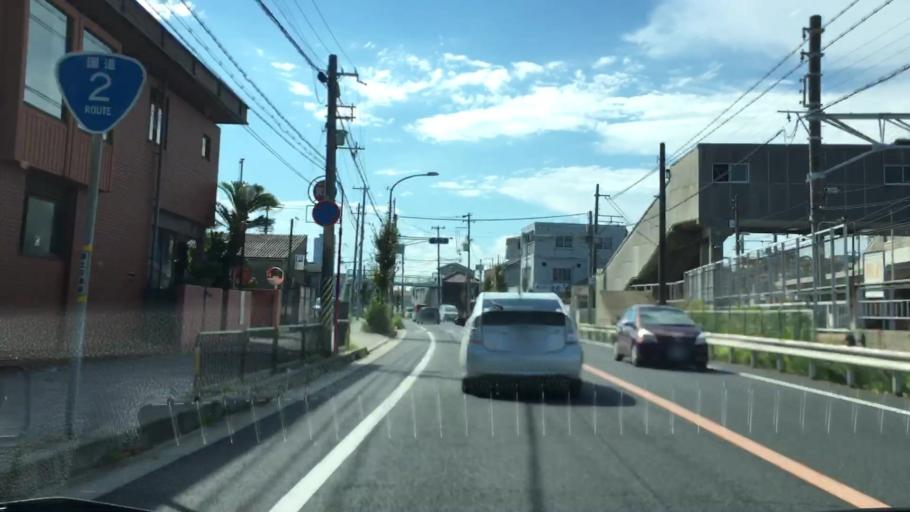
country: JP
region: Hyogo
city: Akashi
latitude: 34.6463
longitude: 135.0088
